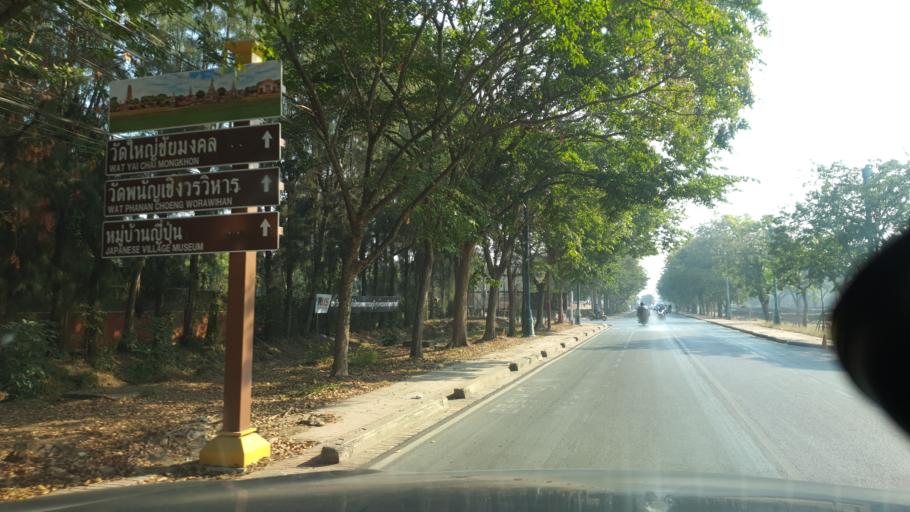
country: TH
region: Phra Nakhon Si Ayutthaya
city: Phra Nakhon Si Ayutthaya
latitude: 14.3577
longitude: 100.5656
